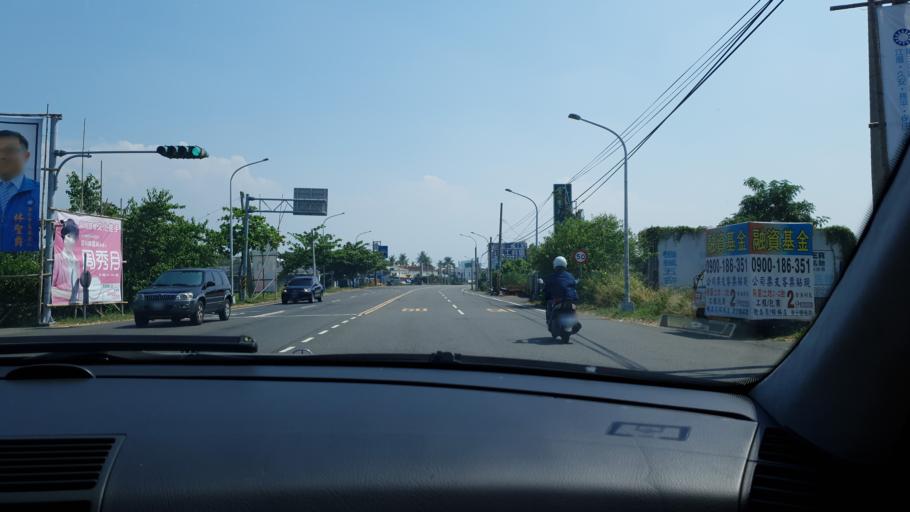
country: TW
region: Taiwan
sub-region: Yunlin
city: Douliu
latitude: 23.7278
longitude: 120.5224
